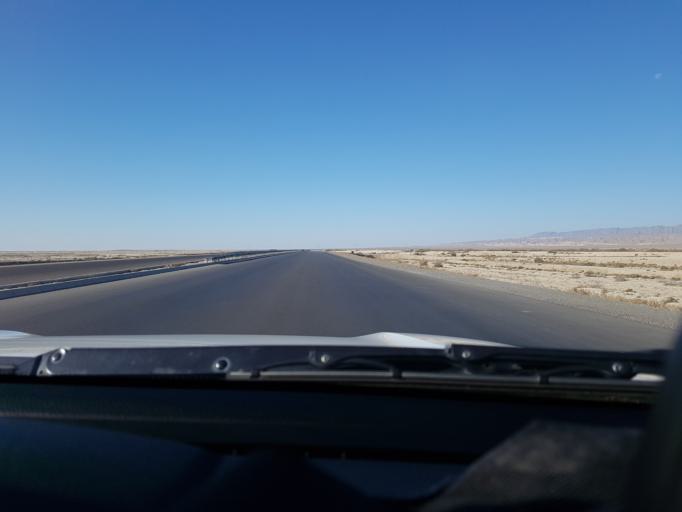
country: TM
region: Balkan
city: Gazanjyk
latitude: 39.2680
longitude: 55.1343
